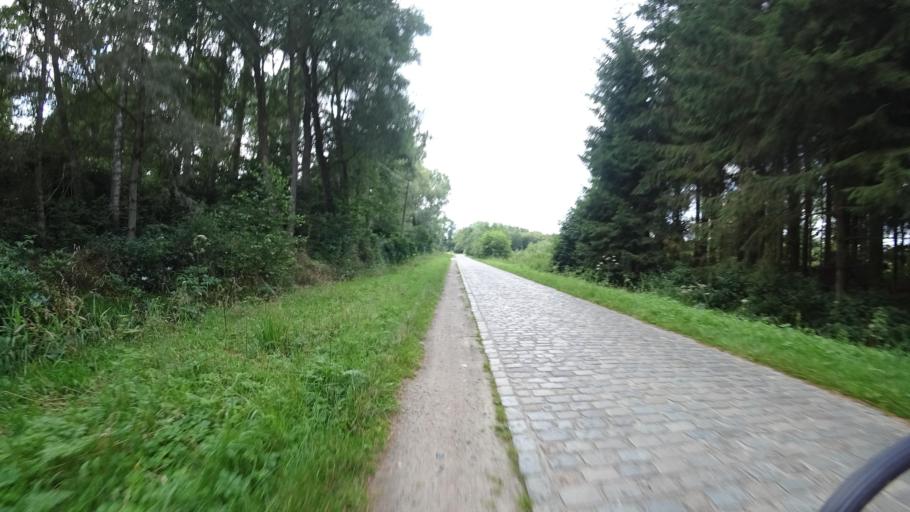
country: BE
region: Flanders
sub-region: Provincie West-Vlaanderen
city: Sint-Kruis
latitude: 51.1913
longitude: 3.2952
